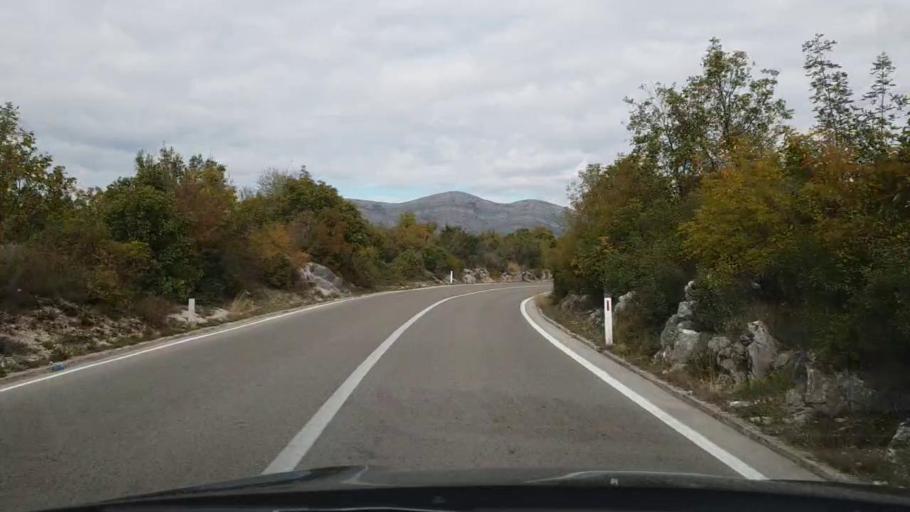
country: HR
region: Dubrovacko-Neretvanska
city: Jasenice
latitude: 42.6869
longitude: 18.2498
